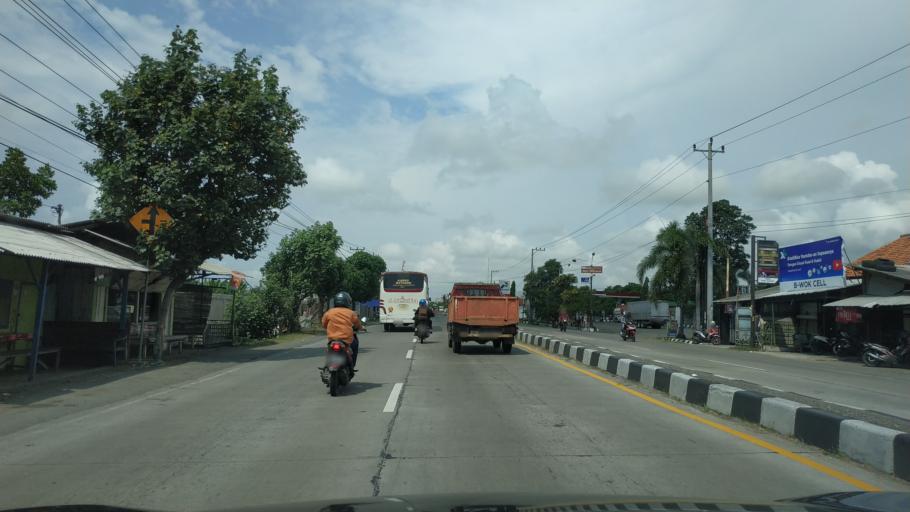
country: ID
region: Central Java
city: Tarub
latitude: -6.8710
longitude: 109.2372
